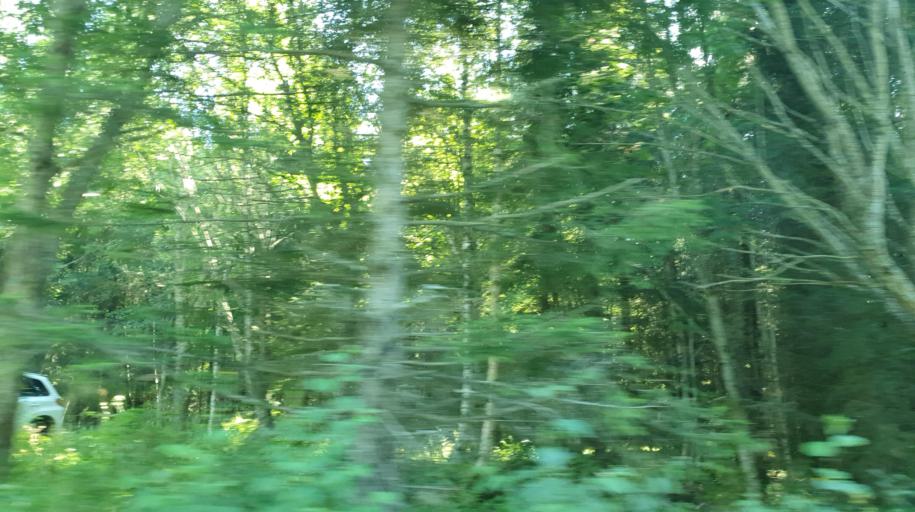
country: NO
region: Nord-Trondelag
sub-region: Levanger
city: Levanger
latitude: 63.6961
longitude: 11.2772
